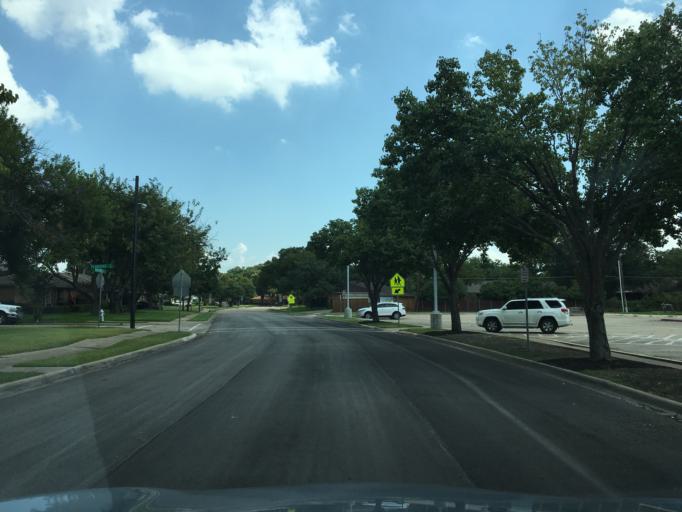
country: US
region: Texas
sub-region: Dallas County
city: Garland
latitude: 32.9350
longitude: -96.6459
